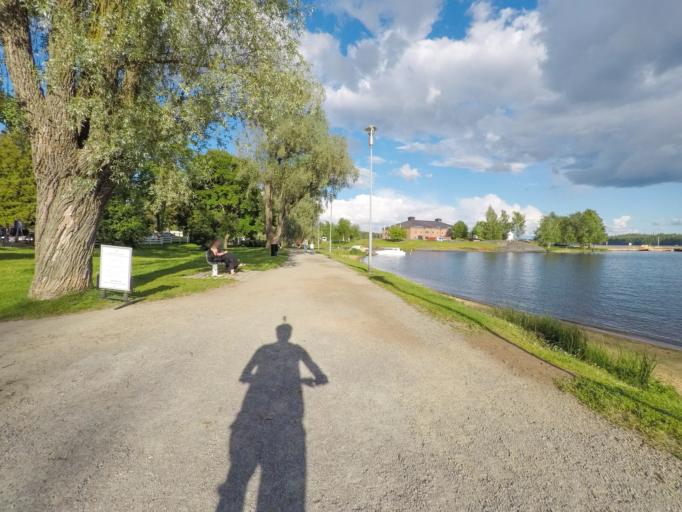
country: FI
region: Southern Savonia
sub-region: Savonlinna
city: Savonlinna
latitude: 61.8644
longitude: 28.8921
